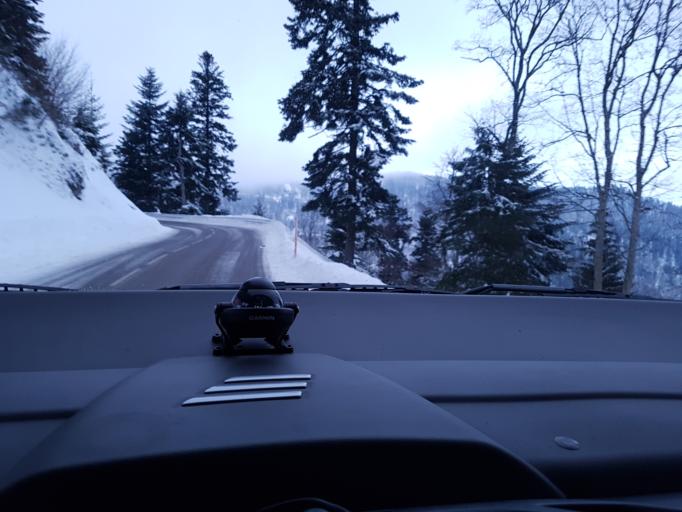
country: FR
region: Alsace
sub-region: Departement du Haut-Rhin
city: Lapoutroie
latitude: 48.1946
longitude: 7.1232
